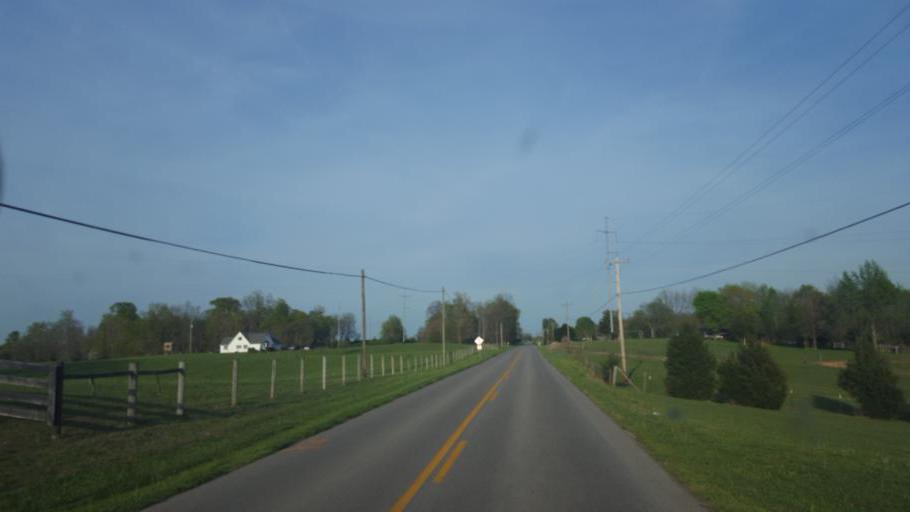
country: US
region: Kentucky
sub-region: Barren County
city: Glasgow
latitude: 36.9449
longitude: -85.9995
